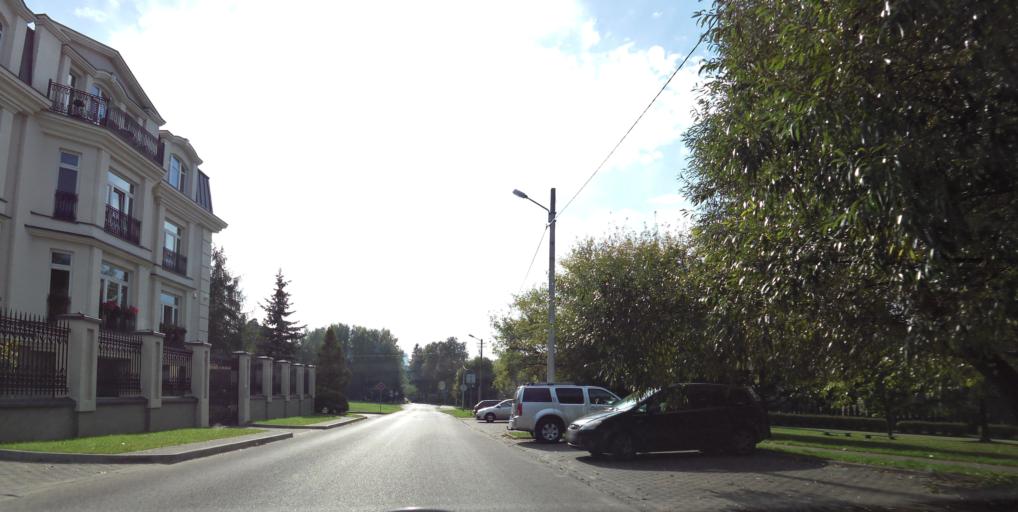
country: LT
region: Vilnius County
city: Seskine
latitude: 54.6908
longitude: 25.2465
